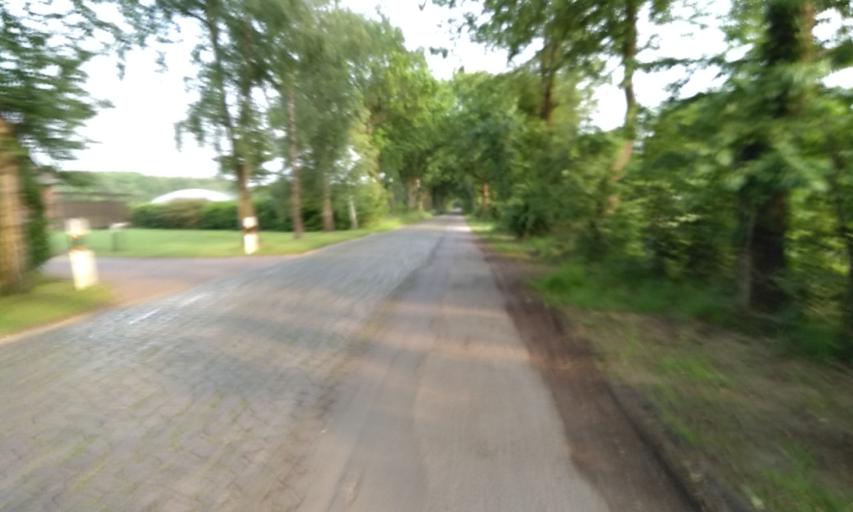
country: DE
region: Lower Saxony
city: Deinste
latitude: 53.5125
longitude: 9.4487
